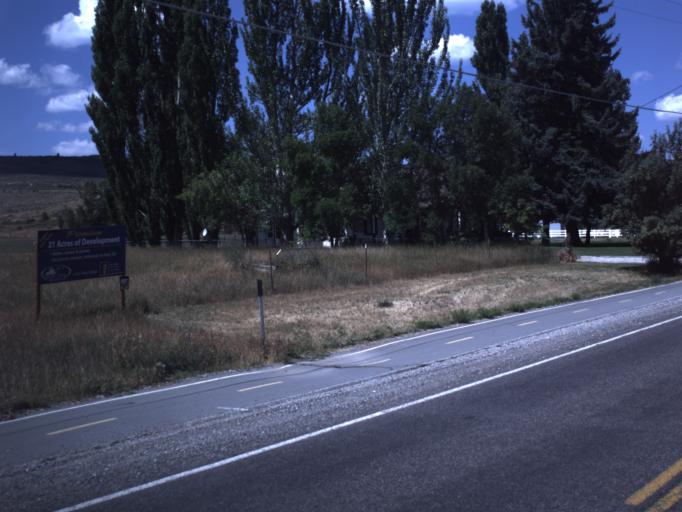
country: US
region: Idaho
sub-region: Bear Lake County
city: Paris
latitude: 41.9154
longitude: -111.3921
